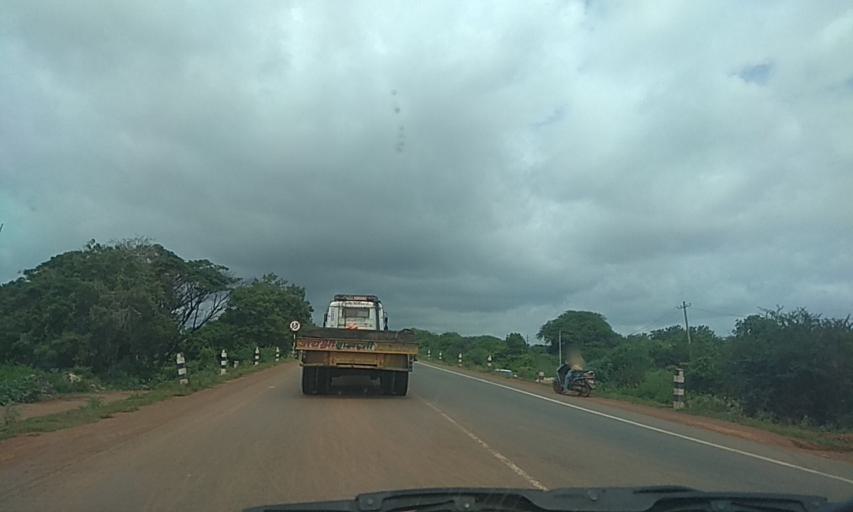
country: IN
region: Karnataka
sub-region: Dharwad
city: Hubli
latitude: 15.3346
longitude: 75.0949
